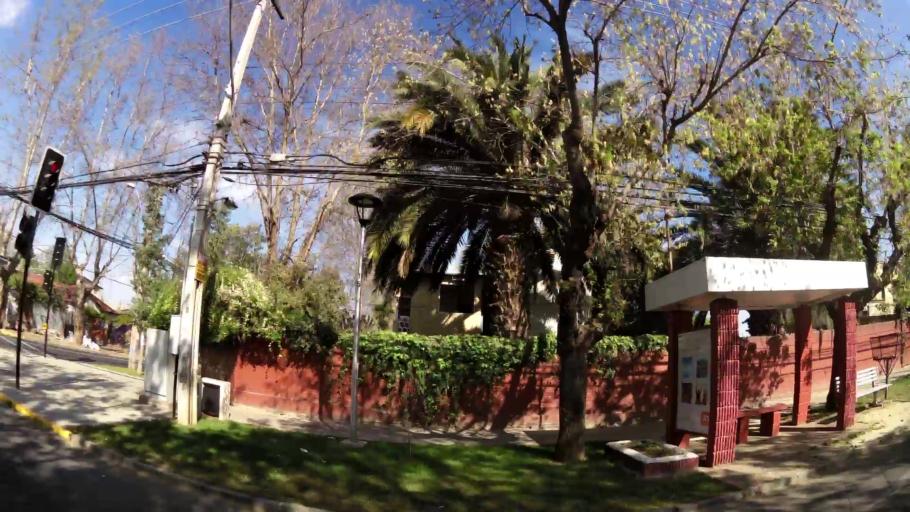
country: CL
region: Santiago Metropolitan
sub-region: Provincia de Santiago
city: Villa Presidente Frei, Nunoa, Santiago, Chile
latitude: -33.4473
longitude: -70.5662
